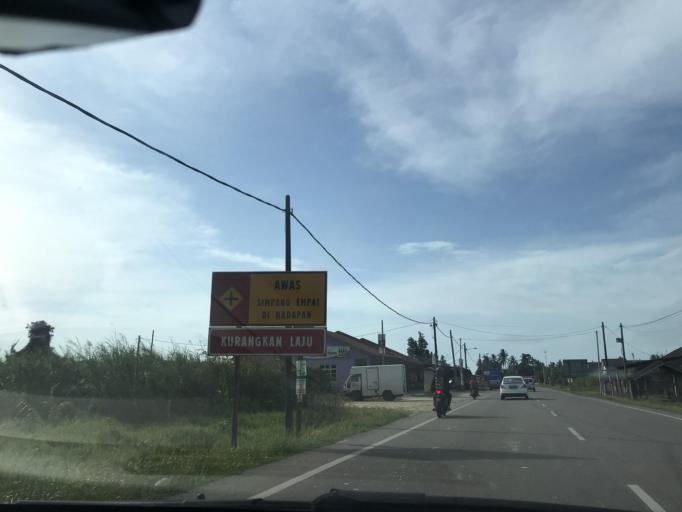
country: MY
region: Kelantan
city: Kota Bharu
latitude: 6.1372
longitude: 102.2025
